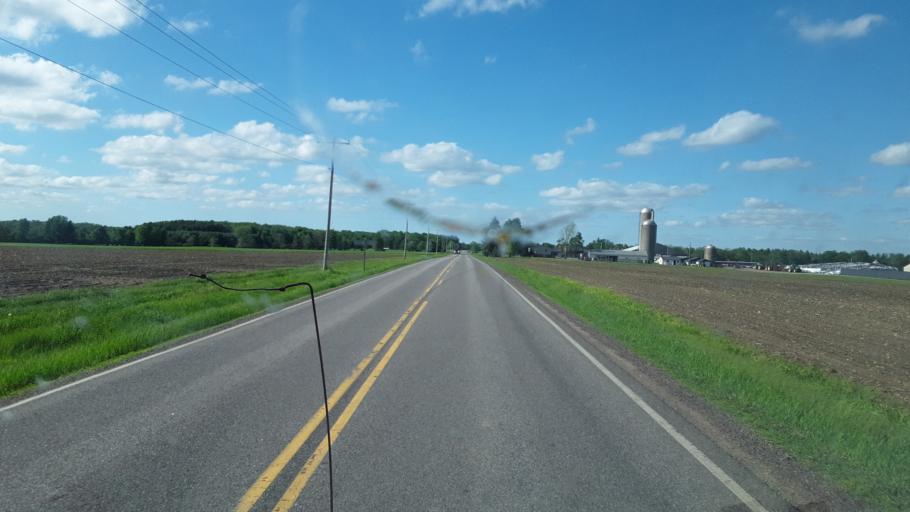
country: US
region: Wisconsin
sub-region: Wood County
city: Marshfield
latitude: 44.4399
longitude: -90.1606
